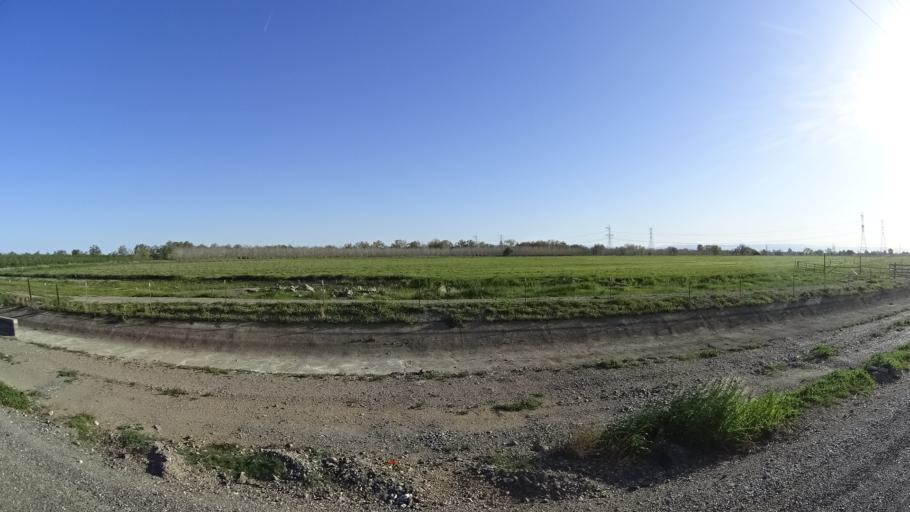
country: US
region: California
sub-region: Glenn County
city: Orland
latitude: 39.7776
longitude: -122.2798
